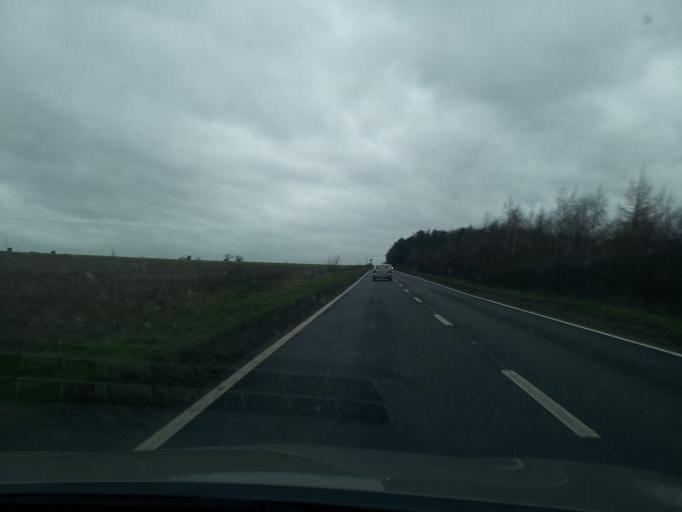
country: GB
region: England
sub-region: Suffolk
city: Ixworth
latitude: 52.2848
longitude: 0.8121
